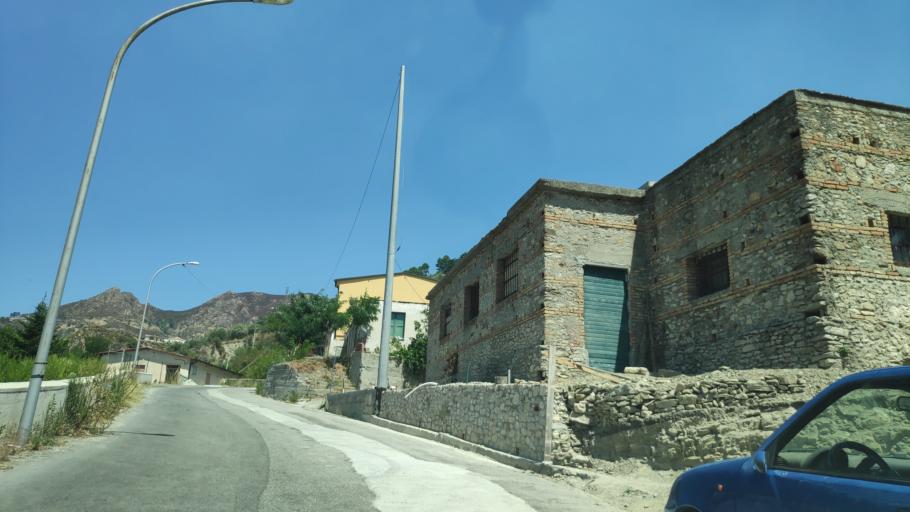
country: IT
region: Calabria
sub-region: Provincia di Reggio Calabria
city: Bova
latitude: 37.9902
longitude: 15.9287
